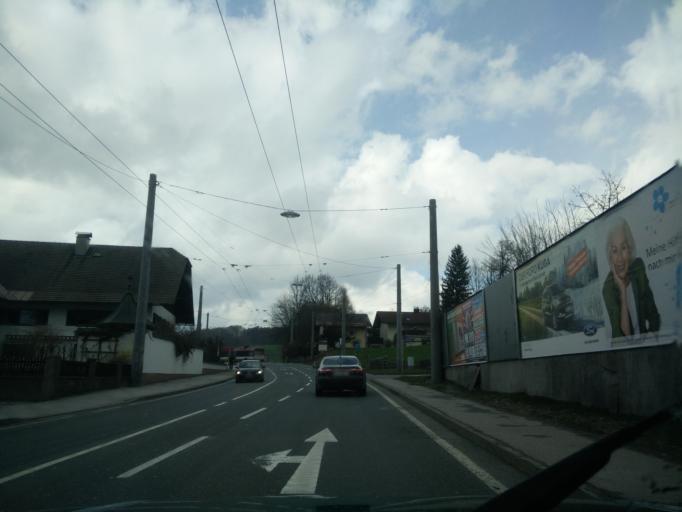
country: AT
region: Salzburg
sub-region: Politischer Bezirk Salzburg-Umgebung
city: Hallwang
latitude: 47.8344
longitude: 13.0874
